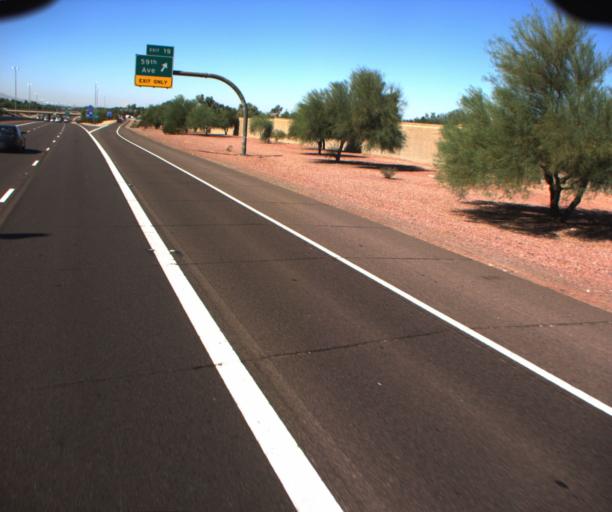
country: US
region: Arizona
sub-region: Maricopa County
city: Peoria
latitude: 33.6685
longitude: -112.1800
